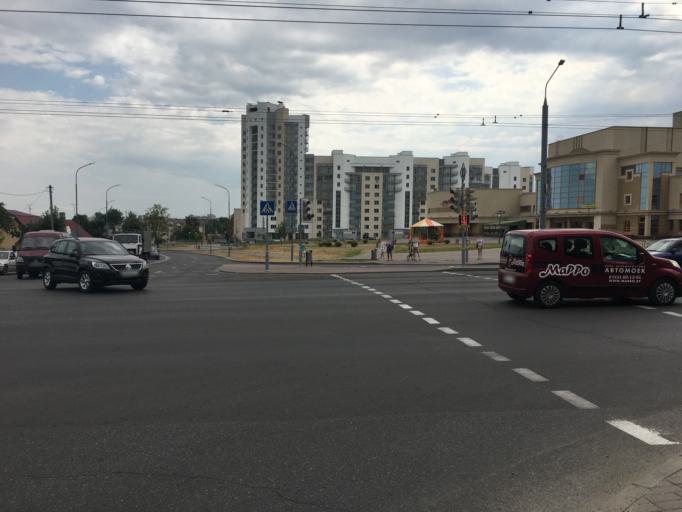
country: BY
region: Grodnenskaya
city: Hrodna
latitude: 53.6753
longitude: 23.8534
